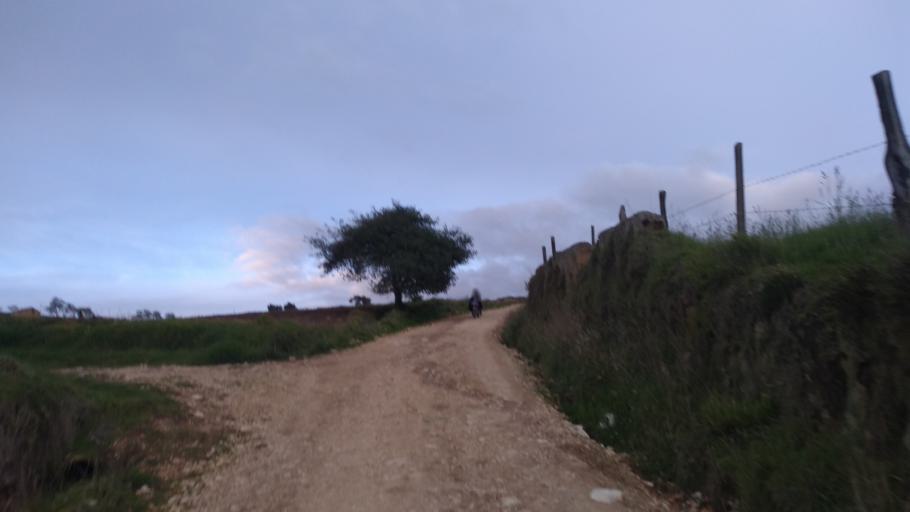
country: CO
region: Boyaca
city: Toca
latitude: 5.5611
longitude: -73.1724
